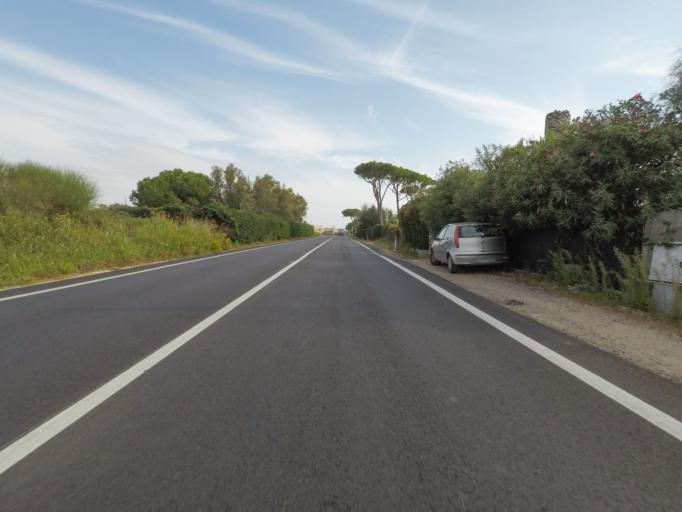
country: IT
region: Latium
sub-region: Citta metropolitana di Roma Capitale
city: Santa Marinella
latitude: 42.0467
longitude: 11.8234
